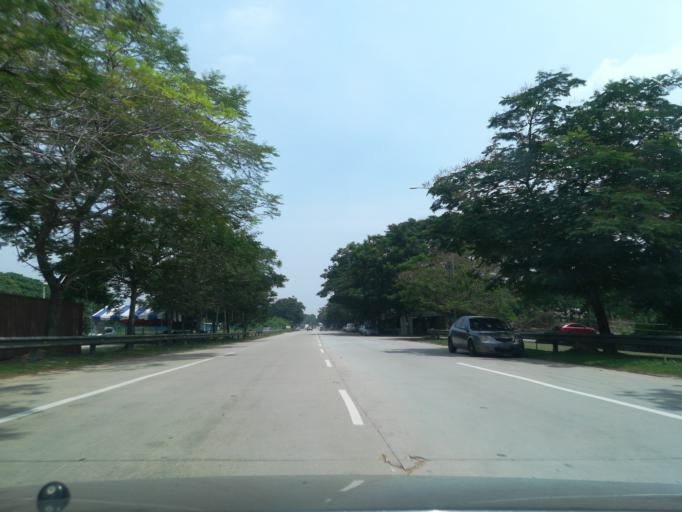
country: MY
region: Kedah
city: Kulim
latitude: 5.4287
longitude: 100.5567
